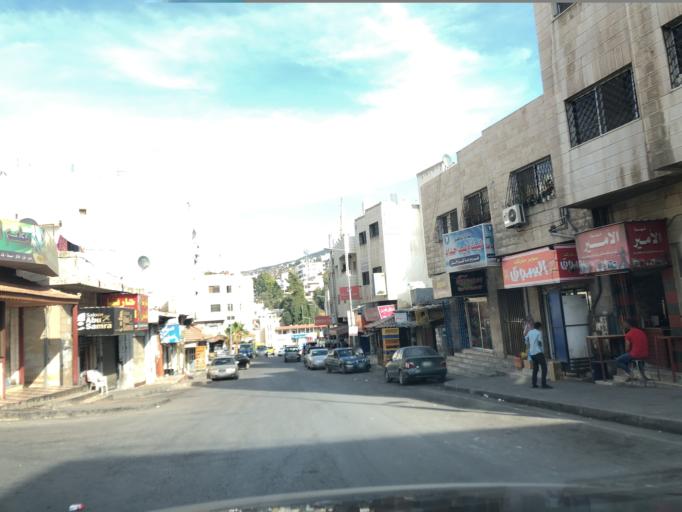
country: JO
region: Ajlun
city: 'Ajlun
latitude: 32.3325
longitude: 35.7495
